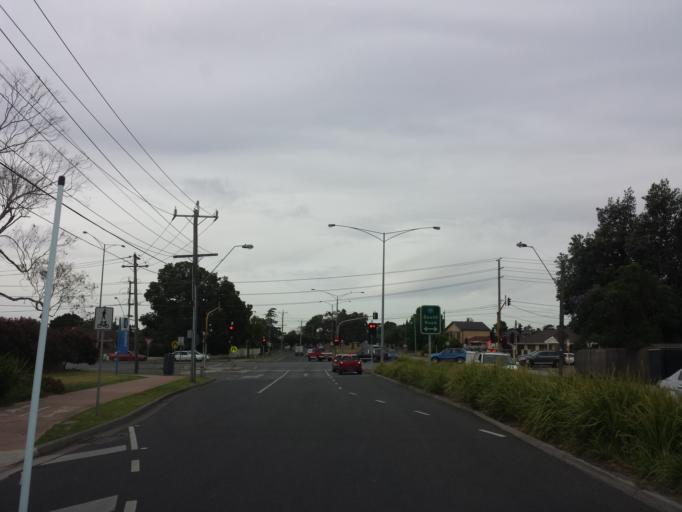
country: AU
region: Victoria
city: Highett
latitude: -37.9364
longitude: 145.0561
